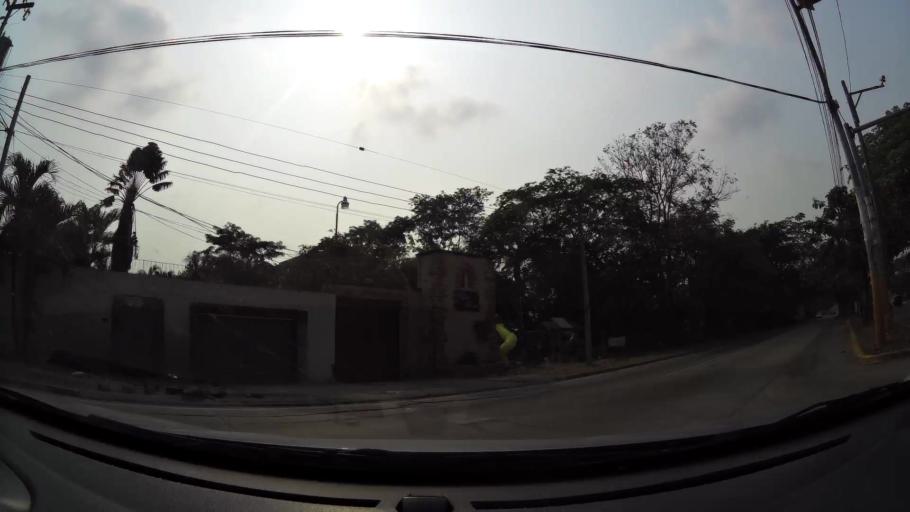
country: HN
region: Cortes
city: El Zapotal del Norte
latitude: 15.5191
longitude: -88.0339
